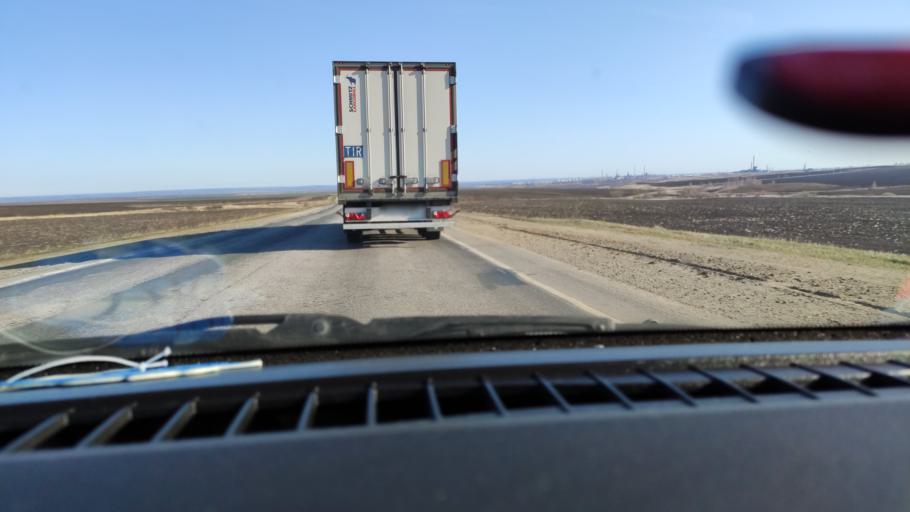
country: RU
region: Samara
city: Syzran'
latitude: 53.0075
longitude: 48.3320
